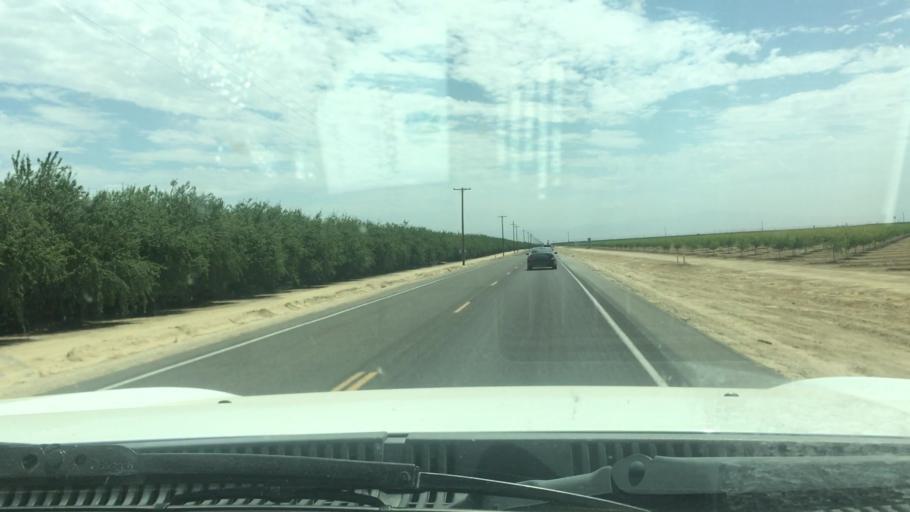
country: US
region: California
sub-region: Kern County
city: Wasco
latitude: 35.5580
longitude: -119.3120
